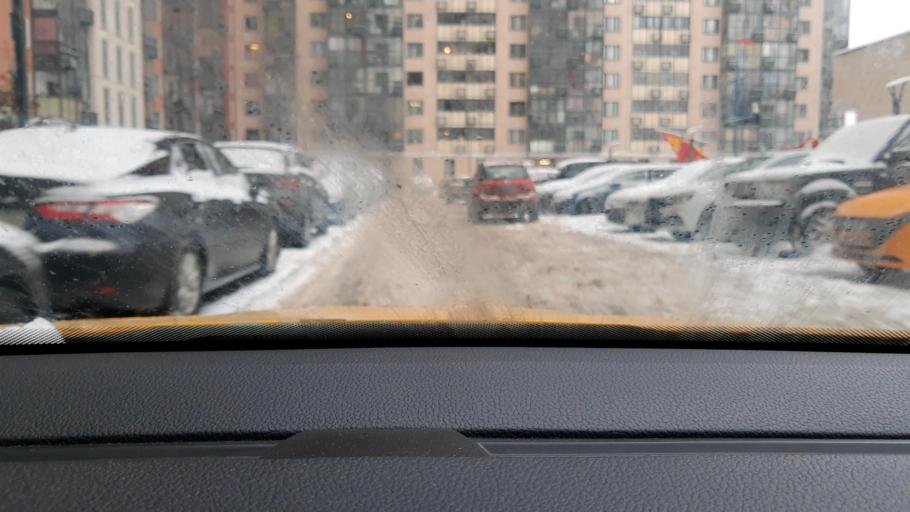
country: RU
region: Moskovskaya
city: Pavshino
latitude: 55.8603
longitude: 37.3729
